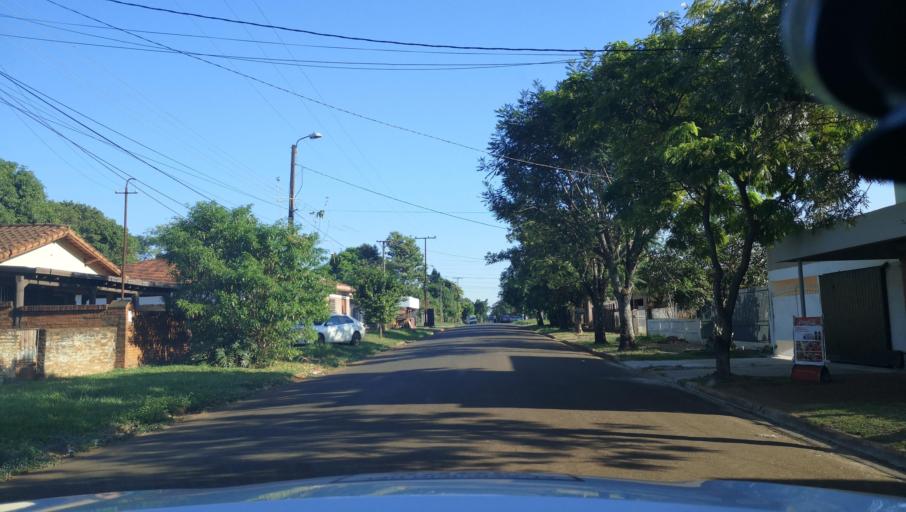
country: PY
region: Itapua
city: Carmen del Parana
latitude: -27.1688
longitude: -56.2428
